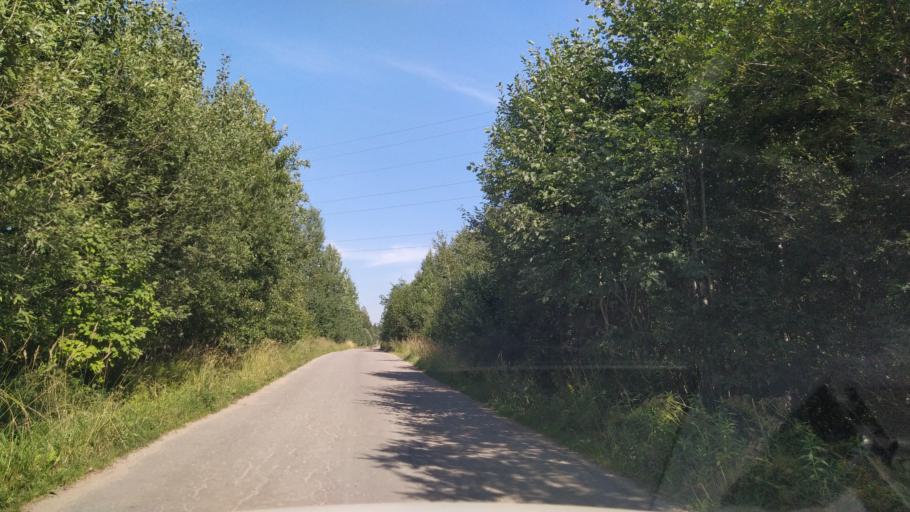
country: RU
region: Leningrad
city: Siverskiy
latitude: 59.2824
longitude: 30.0292
